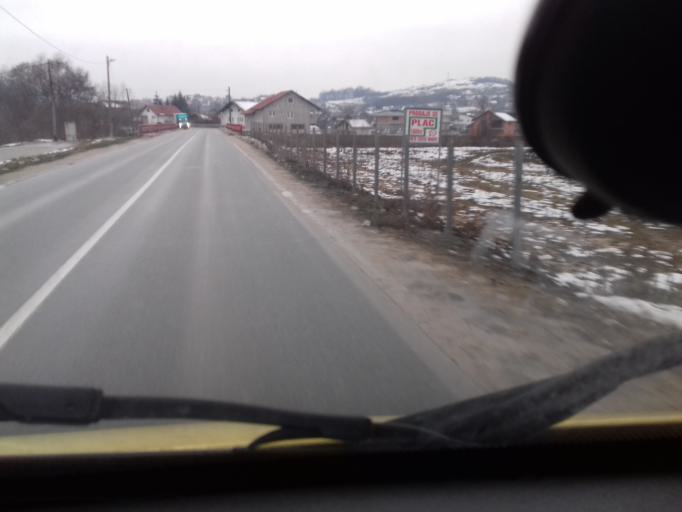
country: BA
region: Federation of Bosnia and Herzegovina
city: Vitez
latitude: 44.1666
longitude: 17.7699
